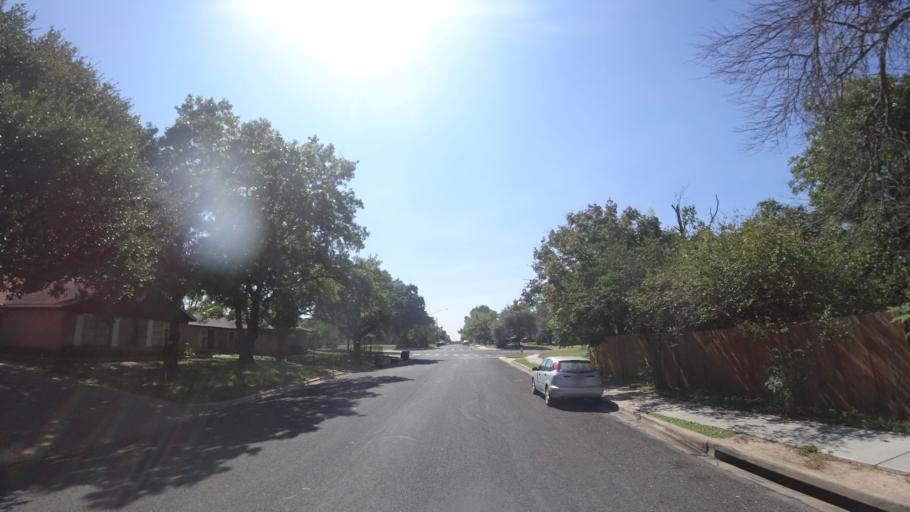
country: US
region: Texas
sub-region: Travis County
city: Austin
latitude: 30.3072
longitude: -97.6855
